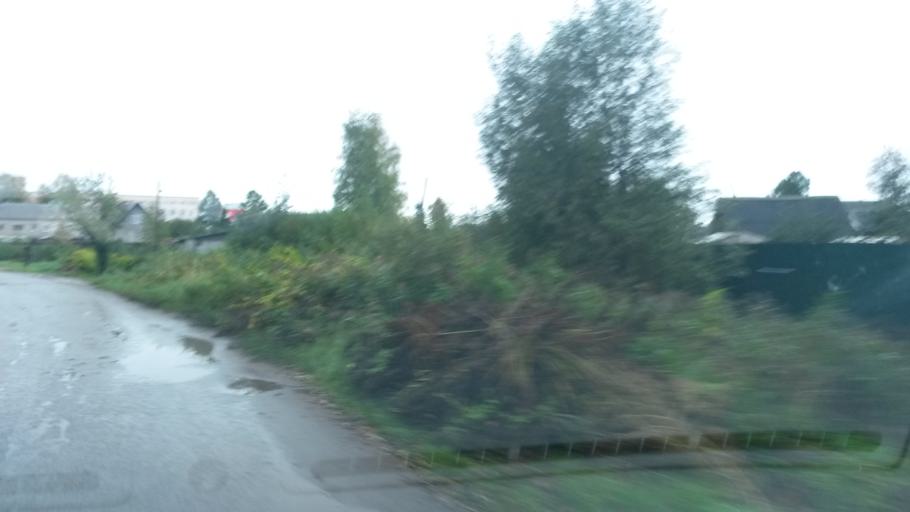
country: RU
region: Jaroslavl
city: Gavrilov-Yam
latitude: 57.3130
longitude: 39.8624
